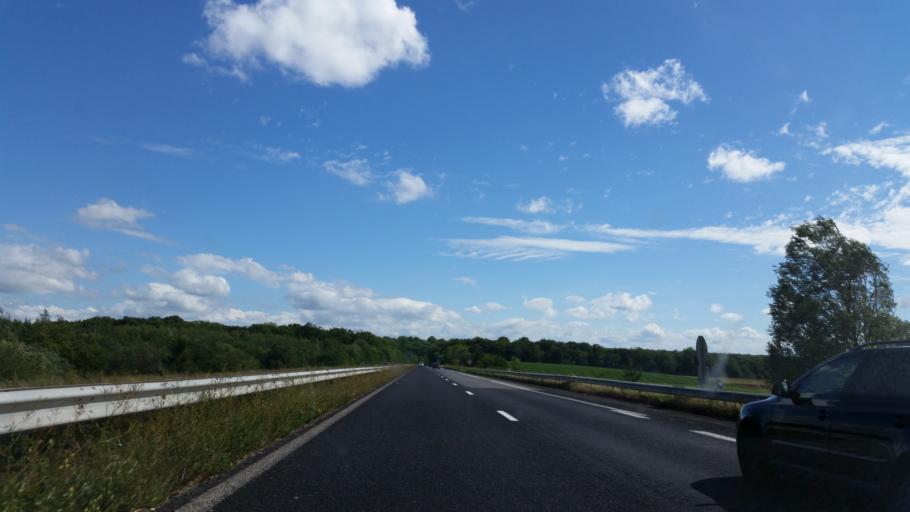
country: FR
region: Lorraine
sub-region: Departement des Vosges
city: Charmes
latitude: 48.4127
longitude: 6.2326
